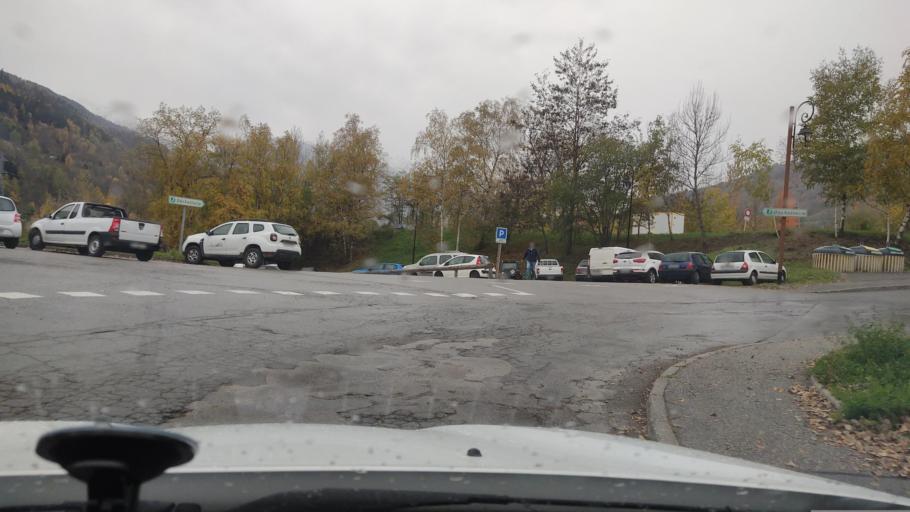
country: FR
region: Rhone-Alpes
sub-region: Departement de la Savoie
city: Bourg-Saint-Maurice
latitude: 45.6092
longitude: 6.7695
